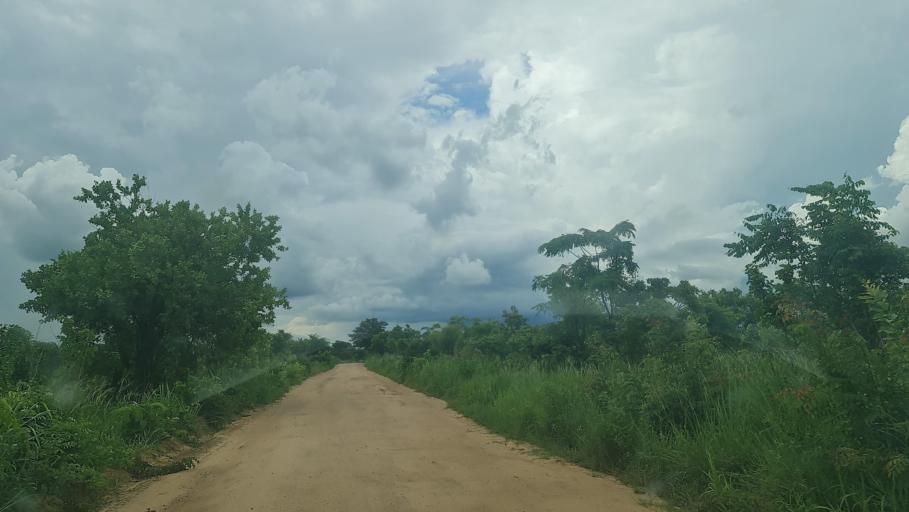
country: MW
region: Southern Region
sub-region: Nsanje District
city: Nsanje
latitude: -17.5718
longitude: 35.6532
